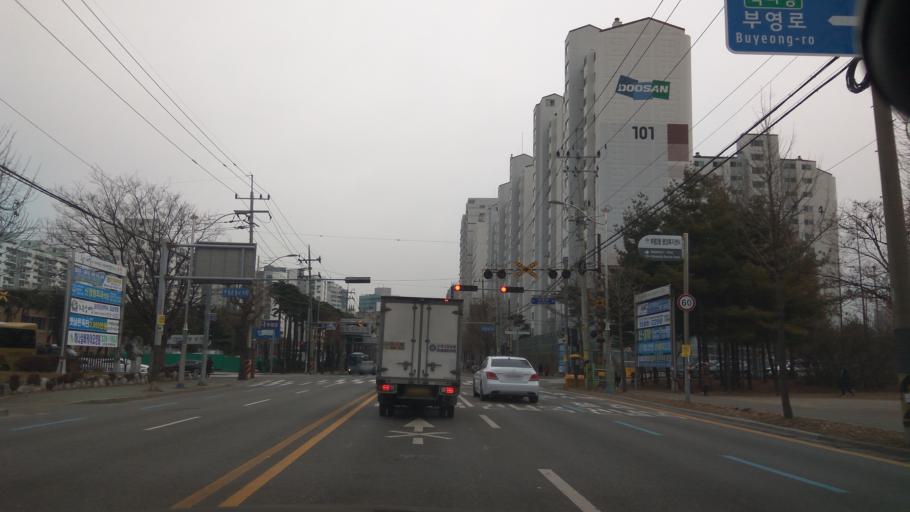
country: KR
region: Incheon
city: Incheon
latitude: 37.4911
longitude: 126.7157
